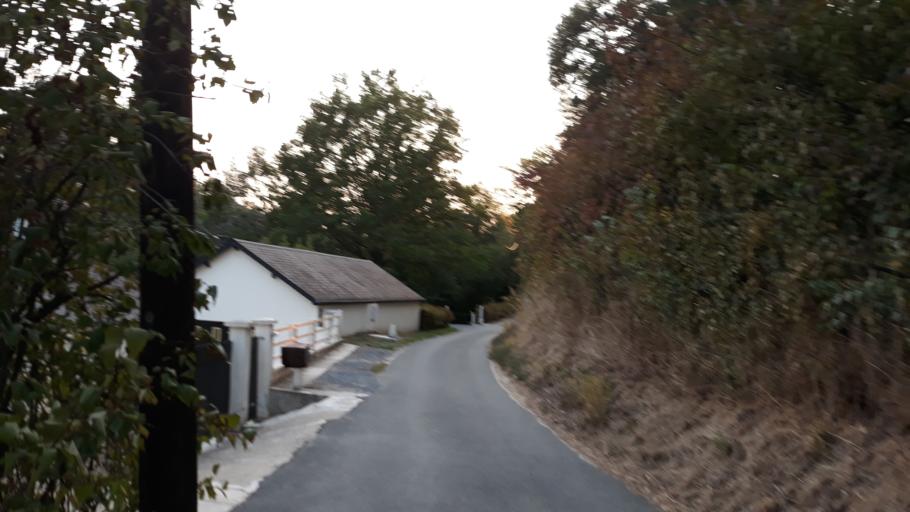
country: FR
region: Picardie
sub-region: Departement de l'Aisne
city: Laon
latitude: 49.5513
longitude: 3.6133
